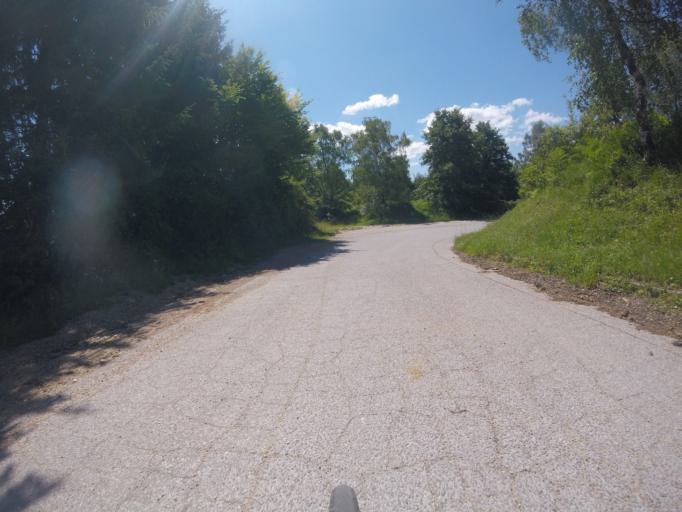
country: SI
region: Kostanjevica na Krki
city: Kostanjevica na Krki
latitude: 45.7771
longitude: 15.4707
